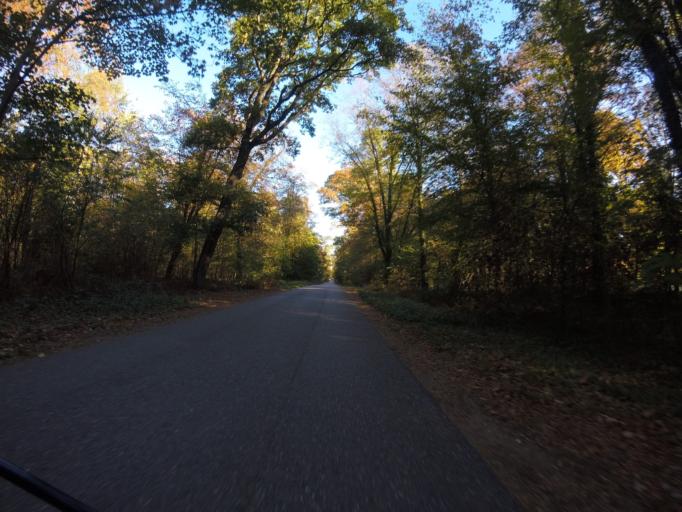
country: DE
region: Baden-Wuerttemberg
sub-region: Karlsruhe Region
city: Karlsruhe
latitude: 49.0258
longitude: 8.4057
